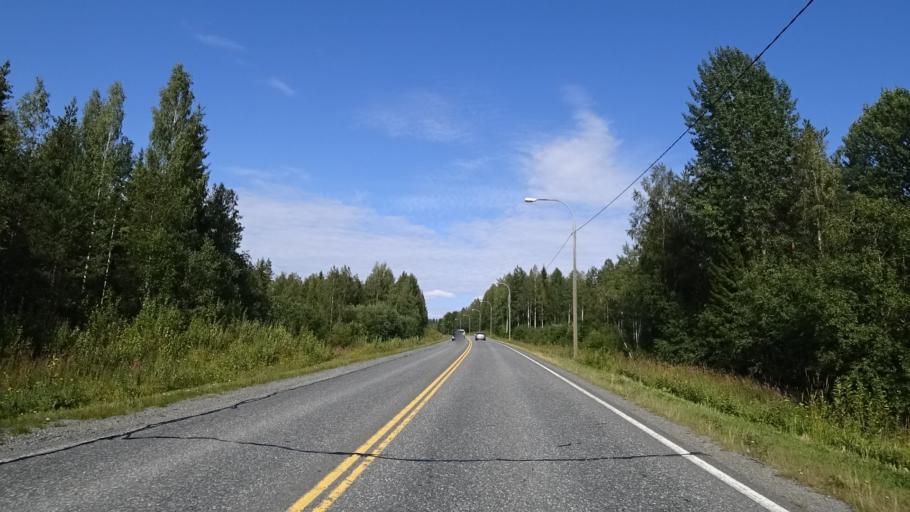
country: FI
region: North Karelia
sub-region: Joensuu
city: Eno
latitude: 62.7806
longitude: 30.0719
